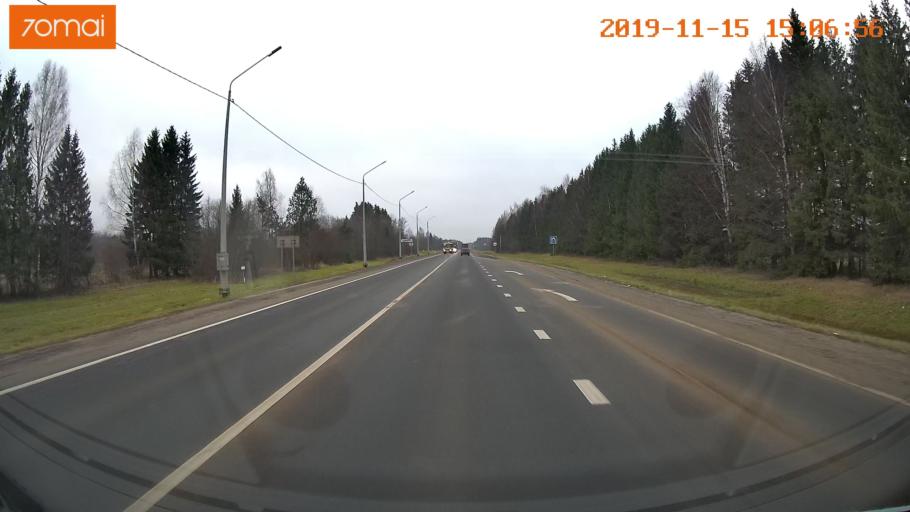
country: RU
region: Jaroslavl
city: Prechistoye
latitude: 58.3886
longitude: 40.3038
